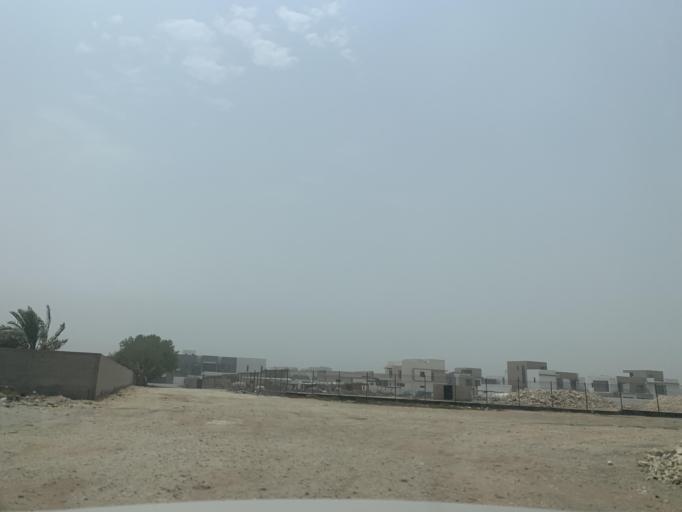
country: BH
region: Central Governorate
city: Madinat Hamad
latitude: 26.1647
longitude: 50.4744
